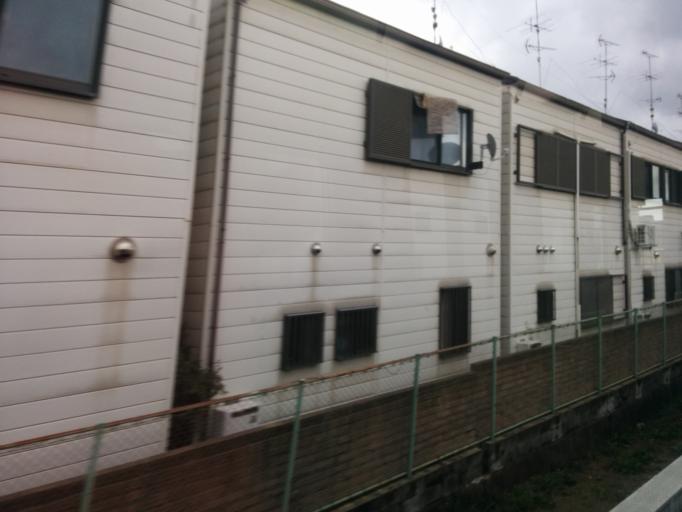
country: JP
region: Kyoto
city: Muko
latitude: 34.9580
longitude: 135.7039
